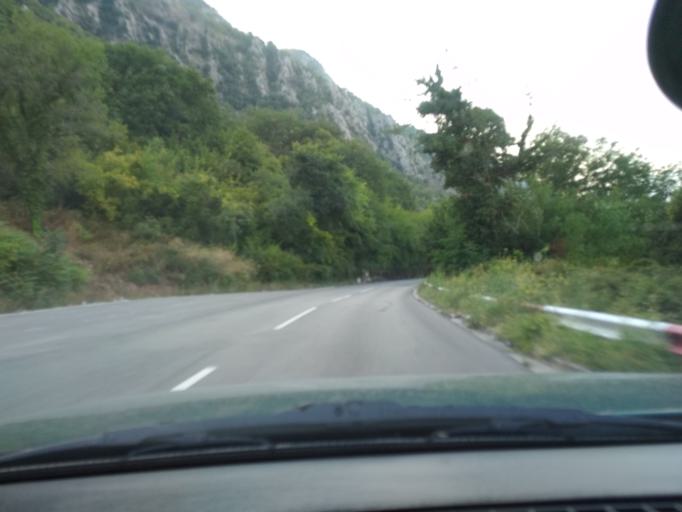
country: ME
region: Kotor
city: Kotor
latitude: 42.4133
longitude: 18.7621
